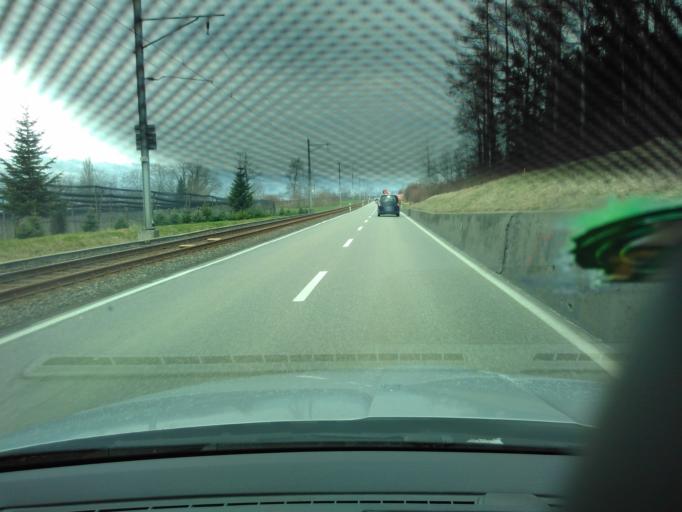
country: CH
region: Lucerne
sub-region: Hochdorf District
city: Hitzkirch
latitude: 47.1989
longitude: 8.2743
